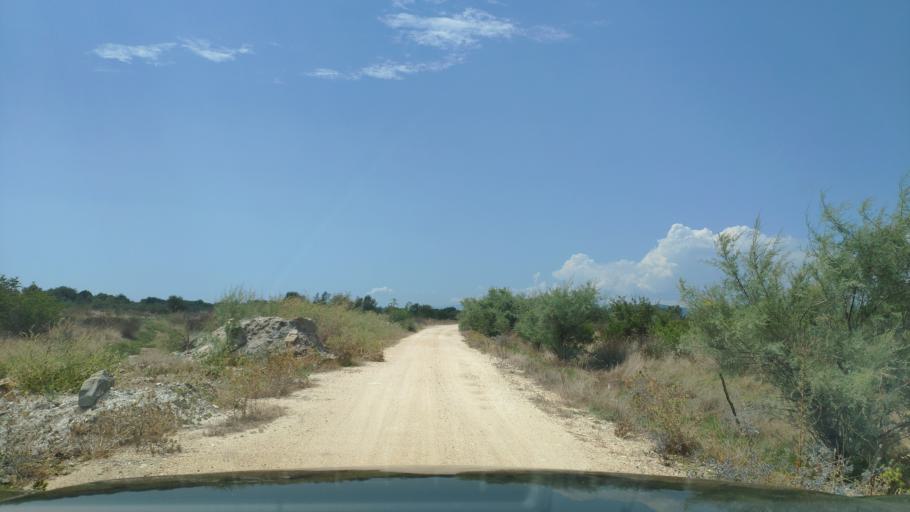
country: GR
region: West Greece
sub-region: Nomos Aitolias kai Akarnanias
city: Menidi
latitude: 39.0534
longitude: 21.0988
